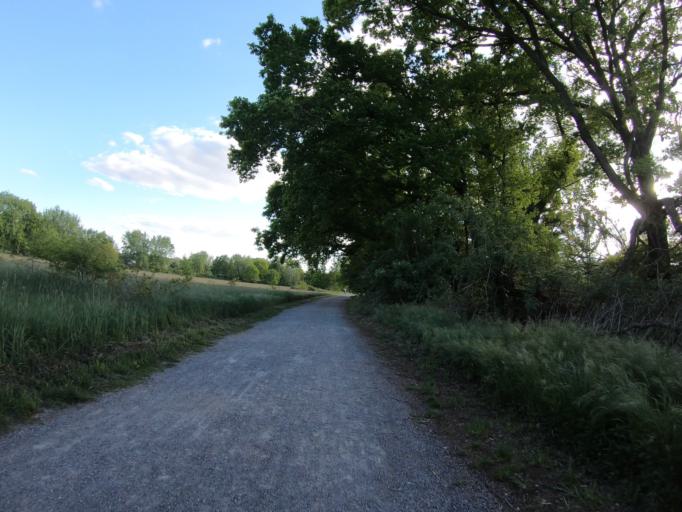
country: DE
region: Lower Saxony
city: Gifhorn
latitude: 52.4877
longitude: 10.5565
